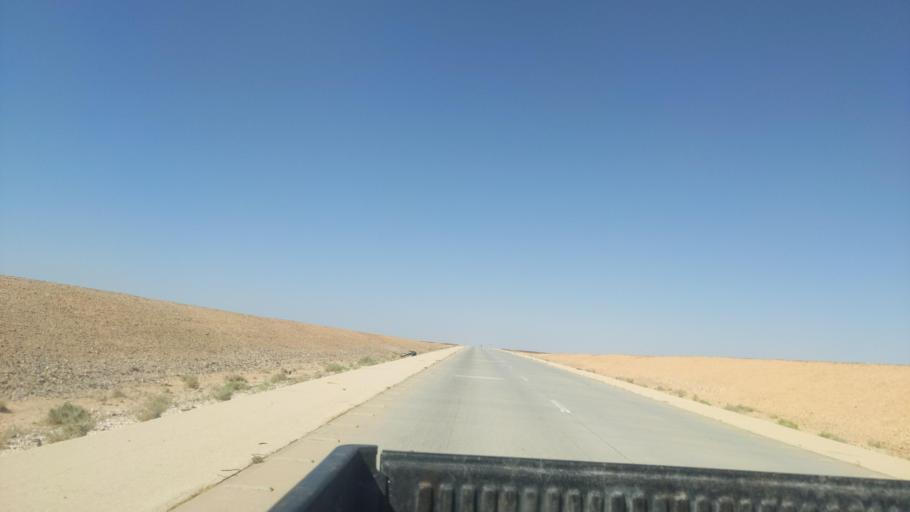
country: JO
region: Amman
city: Al Azraq ash Shamali
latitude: 31.4349
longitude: 36.7440
